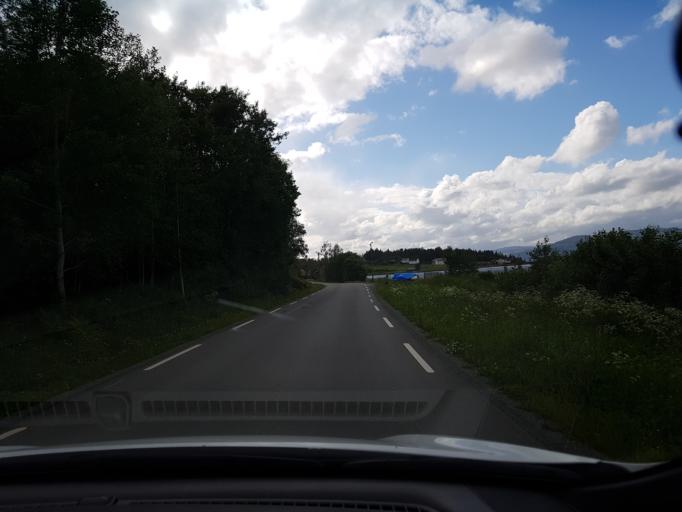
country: NO
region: Nord-Trondelag
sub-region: Frosta
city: Frosta
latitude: 63.6317
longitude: 10.7943
